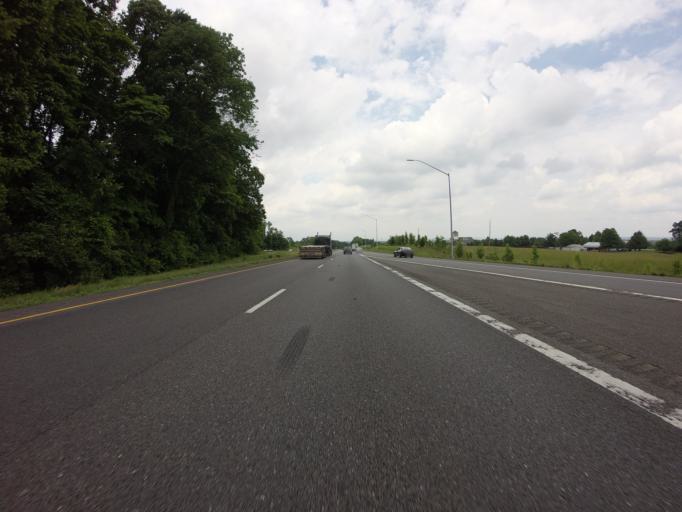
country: US
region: Maryland
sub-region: Frederick County
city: Jefferson
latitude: 39.3659
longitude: -77.5022
